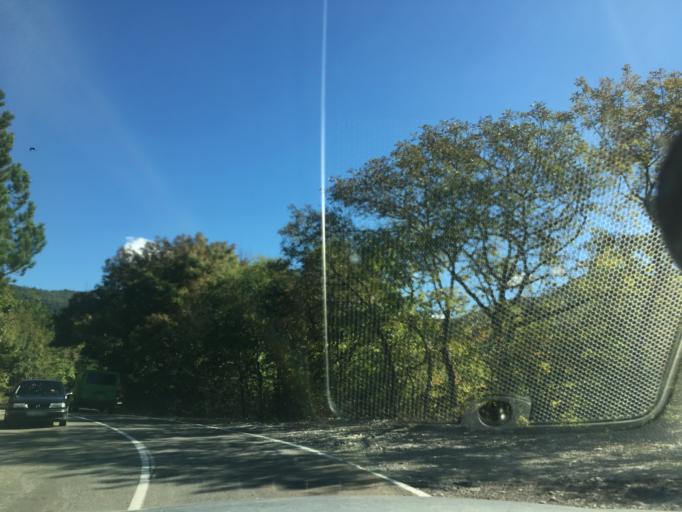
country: GE
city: Didi Lilo
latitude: 41.8595
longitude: 44.9046
